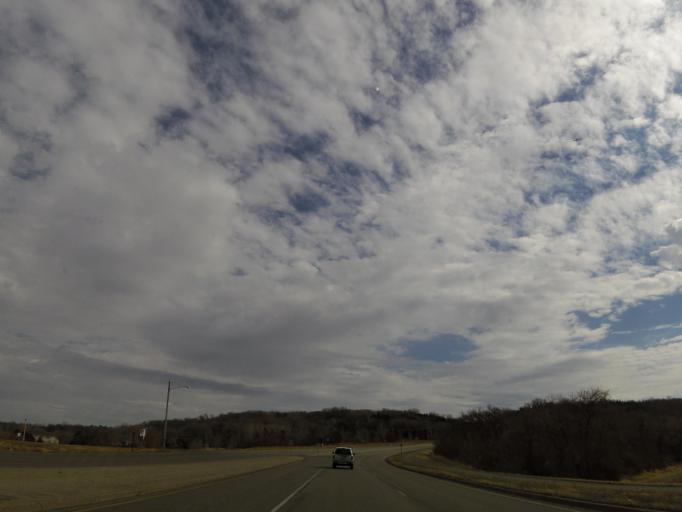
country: US
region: Minnesota
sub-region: Scott County
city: Prior Lake
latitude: 44.7682
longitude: -93.4072
